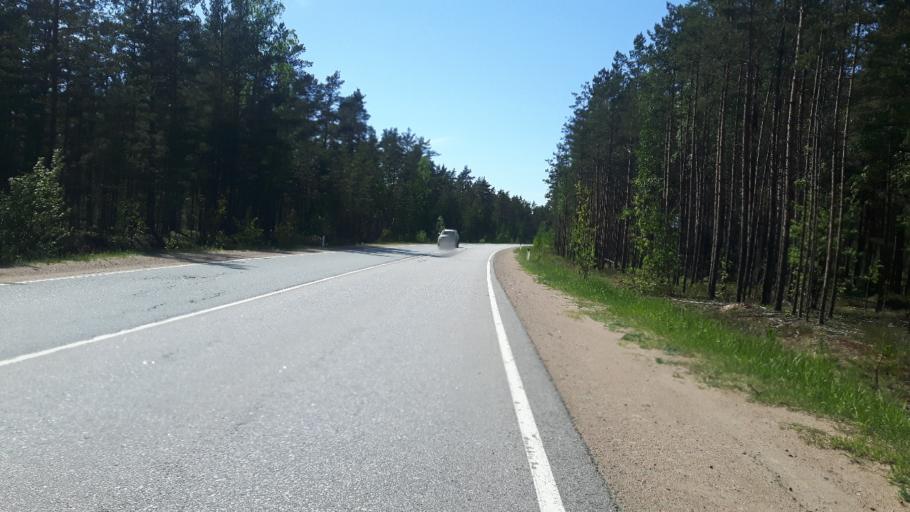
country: RU
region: Leningrad
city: Sista-Palkino
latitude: 59.7678
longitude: 28.8018
